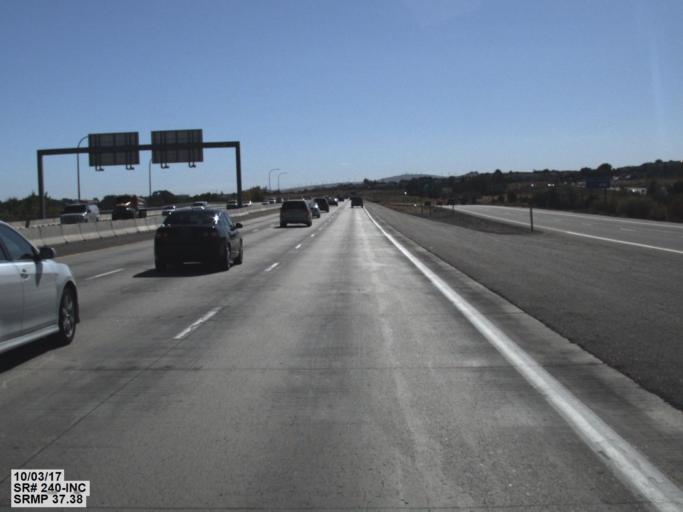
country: US
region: Washington
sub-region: Benton County
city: Richland
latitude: 46.2433
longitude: -119.2483
